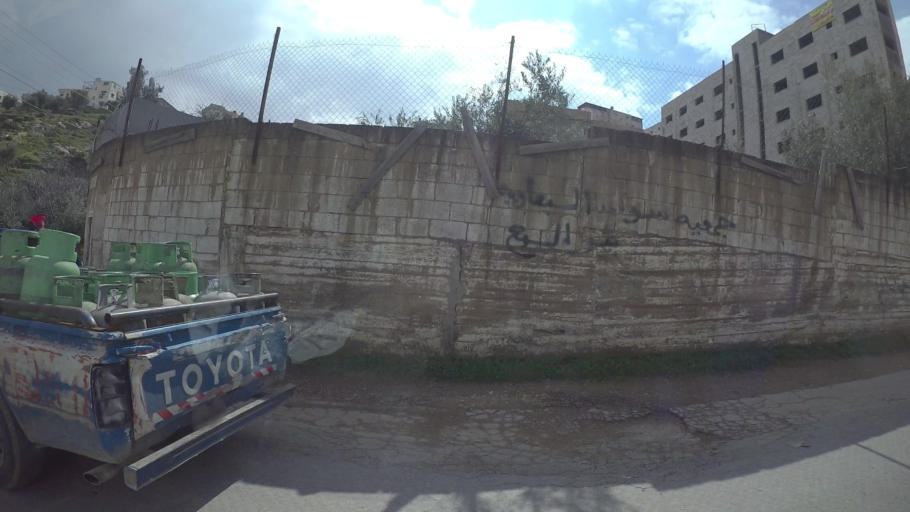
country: JO
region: Amman
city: Al Jubayhah
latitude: 32.0345
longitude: 35.8274
